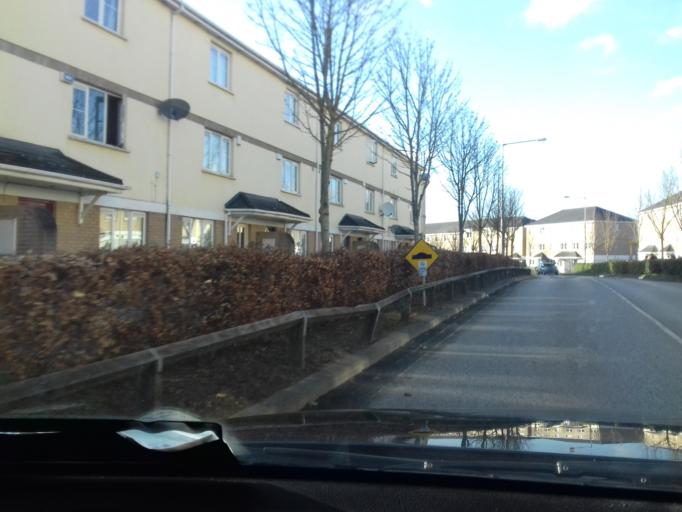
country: IE
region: Leinster
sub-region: Fingal County
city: Blanchardstown
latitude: 53.4171
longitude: -6.3858
